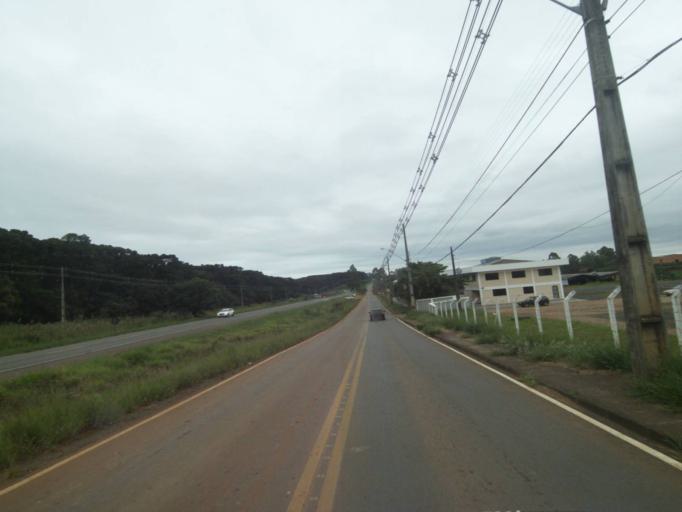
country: BR
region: Parana
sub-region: Telemaco Borba
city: Telemaco Borba
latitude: -24.3602
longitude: -50.6586
